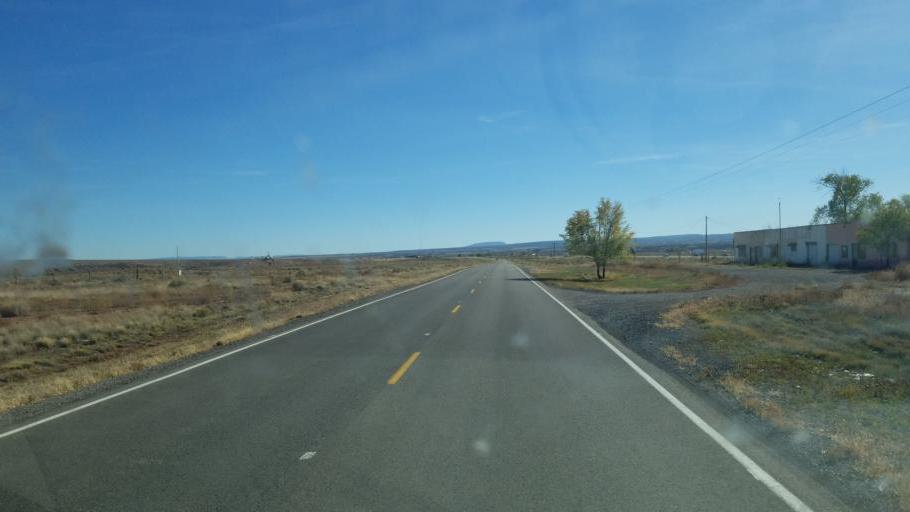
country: US
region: New Mexico
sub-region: Cibola County
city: Milan
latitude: 35.2952
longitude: -107.9869
